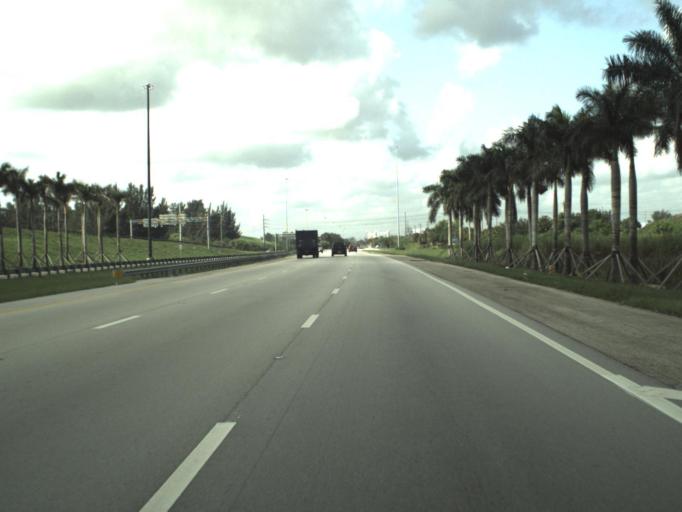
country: US
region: Florida
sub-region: Broward County
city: Broadview Park
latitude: 26.0833
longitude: -80.2036
